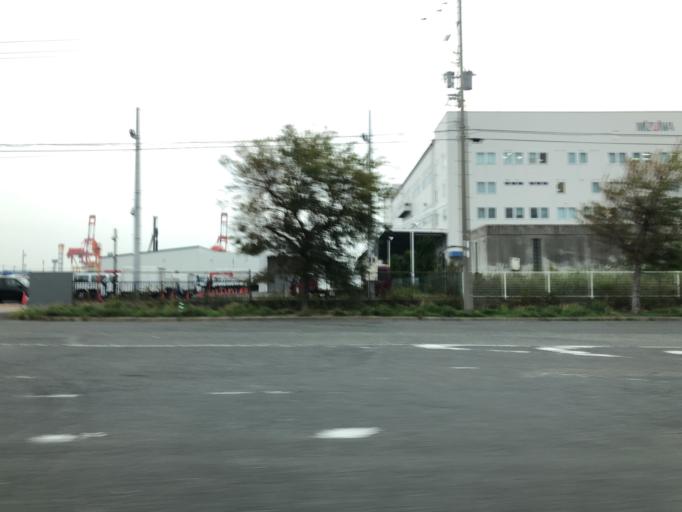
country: JP
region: Hyogo
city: Ashiya
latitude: 34.6840
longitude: 135.2617
